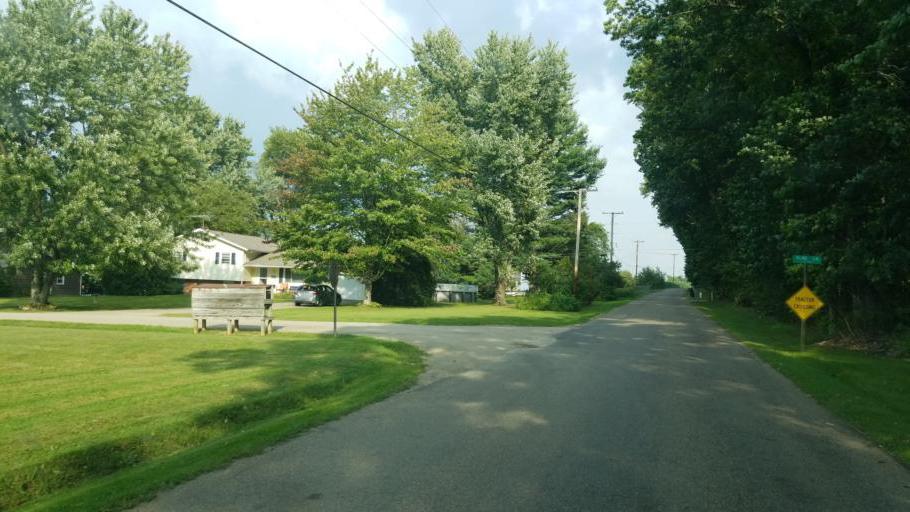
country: US
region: Ohio
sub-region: Knox County
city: Mount Vernon
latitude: 40.3688
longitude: -82.4491
